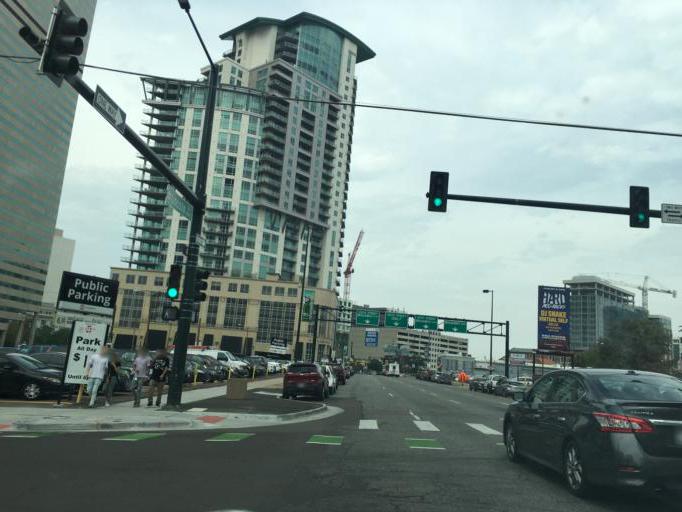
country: US
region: Colorado
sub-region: Denver County
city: Denver
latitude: 39.7462
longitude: -104.9862
